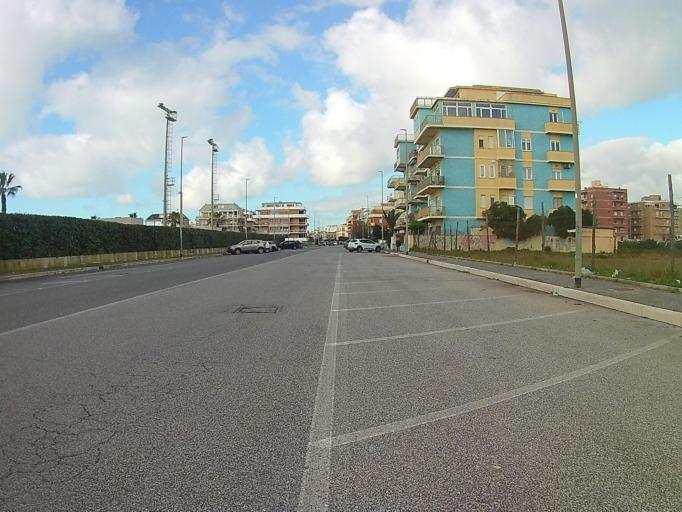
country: IT
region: Latium
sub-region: Citta metropolitana di Roma Capitale
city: Lido di Ostia
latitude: 41.7225
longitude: 12.2983
